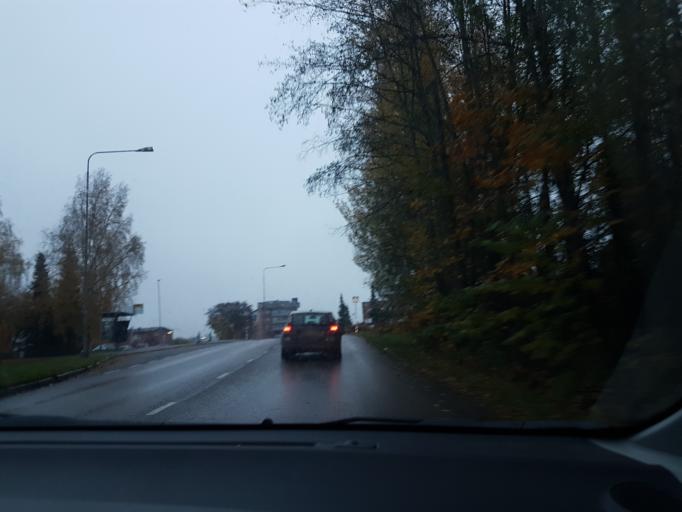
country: FI
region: Uusimaa
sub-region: Helsinki
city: Tuusula
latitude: 60.4035
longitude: 25.0226
